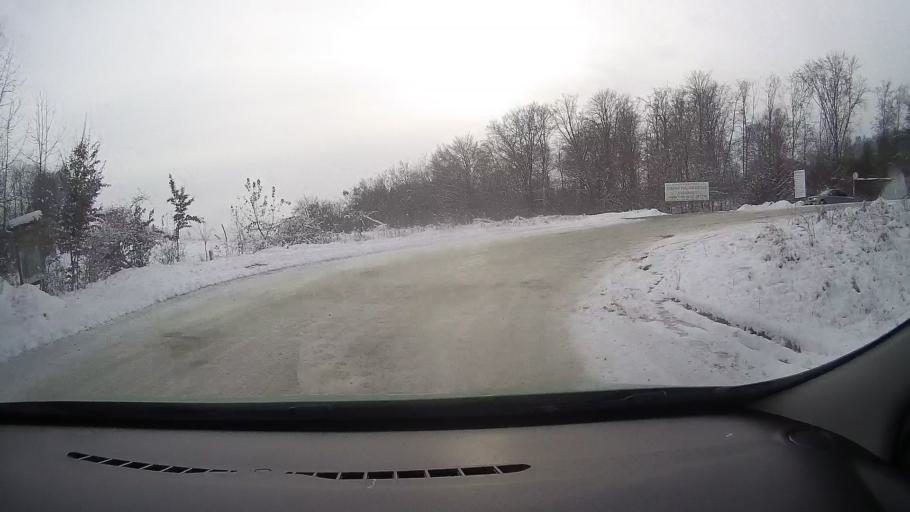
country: RO
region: Alba
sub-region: Comuna Almasu Mare
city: Almasu Mare
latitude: 46.0934
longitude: 23.1688
